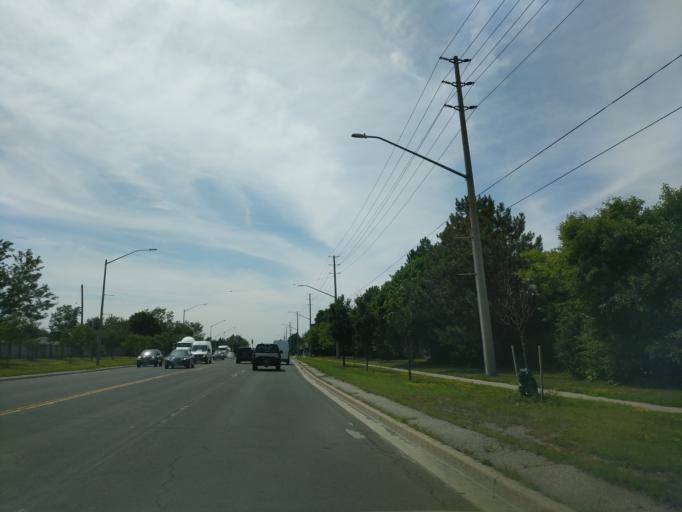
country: CA
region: Ontario
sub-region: York
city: Richmond Hill
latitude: 43.8674
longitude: -79.4551
